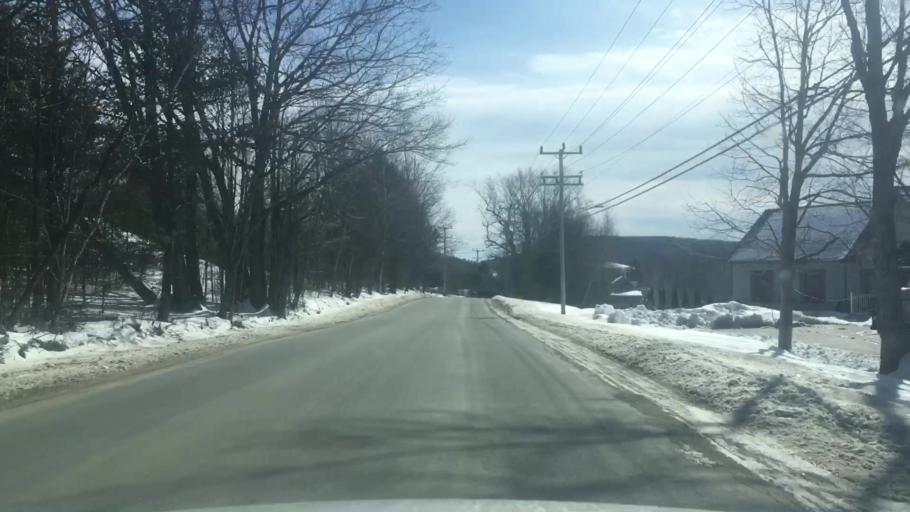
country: US
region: Maine
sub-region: Penobscot County
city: Holden
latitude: 44.7425
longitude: -68.6297
